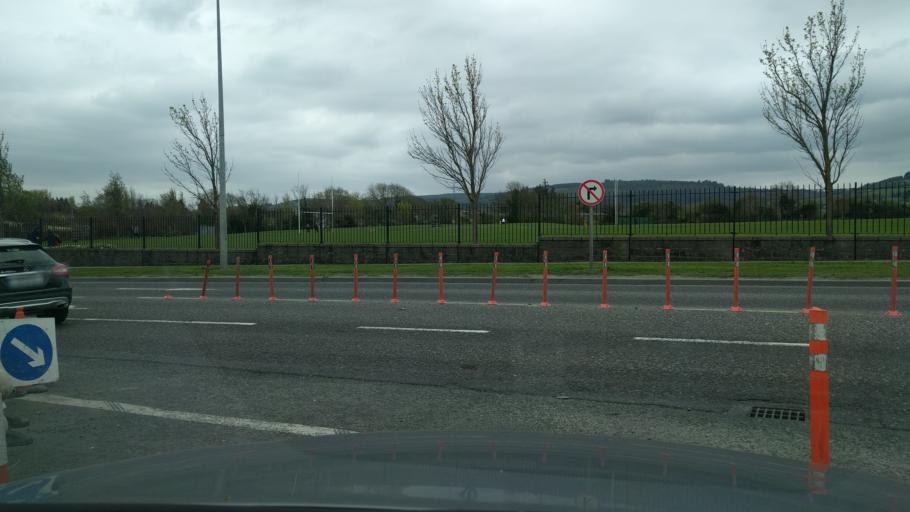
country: IE
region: Leinster
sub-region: South Dublin
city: Saggart
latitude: 53.2836
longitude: -6.4569
